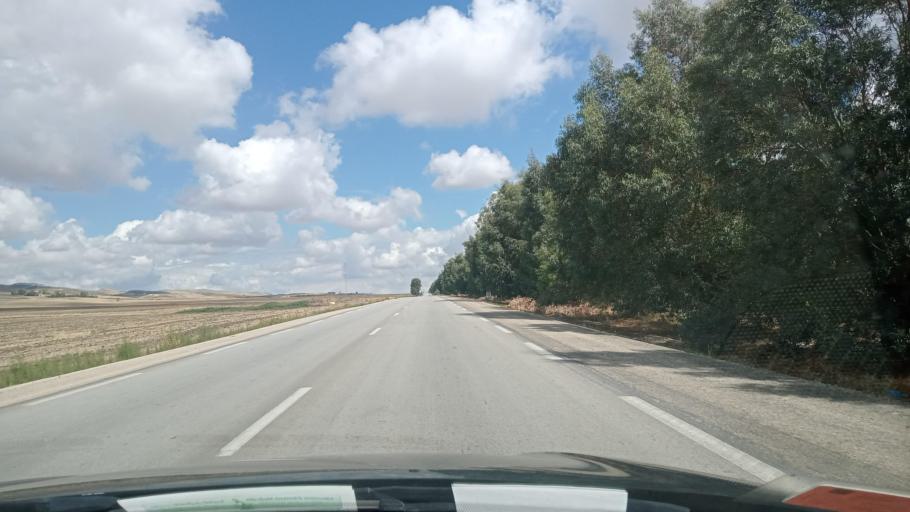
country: TN
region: Silyanah
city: Al Karib
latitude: 36.3092
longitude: 9.0978
